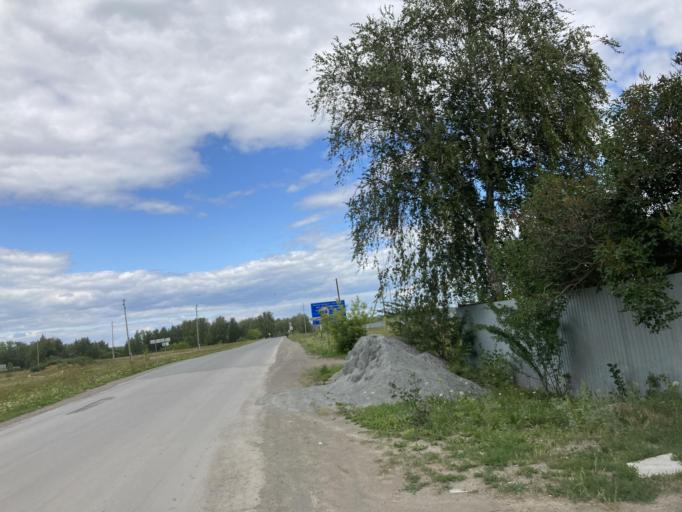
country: RU
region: Sverdlovsk
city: Bogdanovich
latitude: 56.7919
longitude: 62.0677
